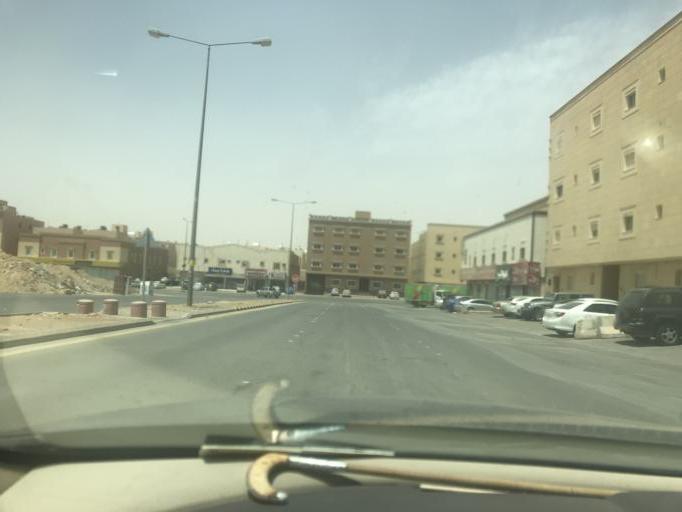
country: SA
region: Ar Riyad
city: Riyadh
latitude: 24.7988
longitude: 46.6662
